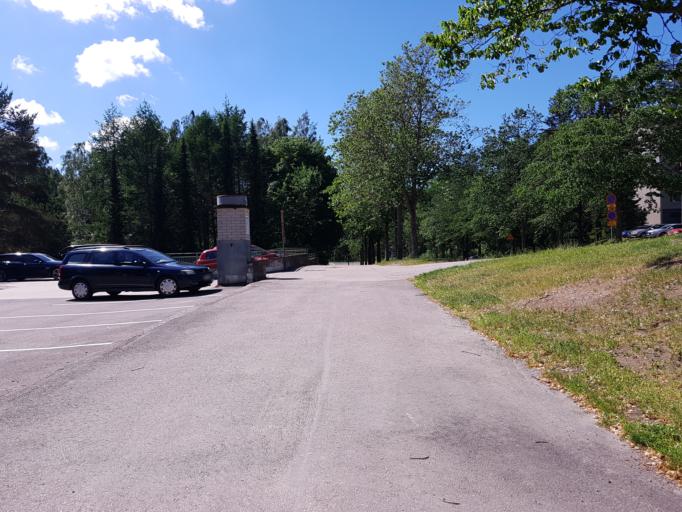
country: FI
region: Uusimaa
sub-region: Helsinki
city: Teekkarikylae
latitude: 60.2668
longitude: 24.8448
